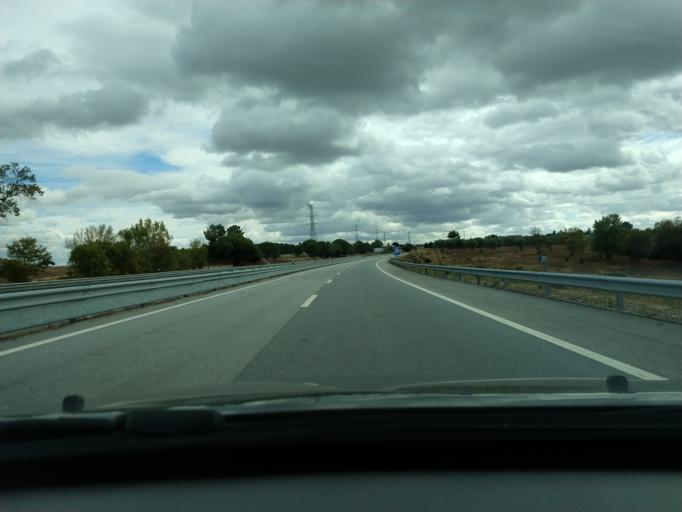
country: PT
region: Guarda
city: Alcains
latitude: 40.0069
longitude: -7.4639
